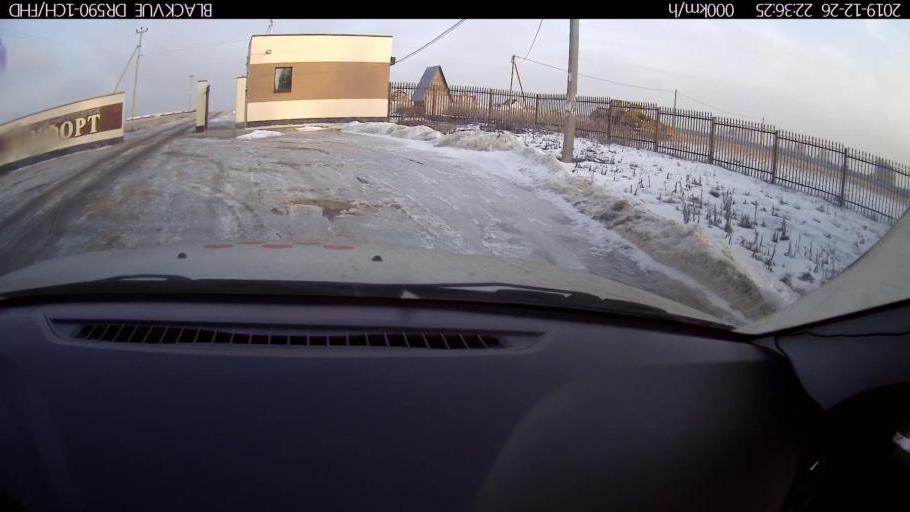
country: RU
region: Nizjnij Novgorod
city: Burevestnik
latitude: 56.1460
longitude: 43.7220
